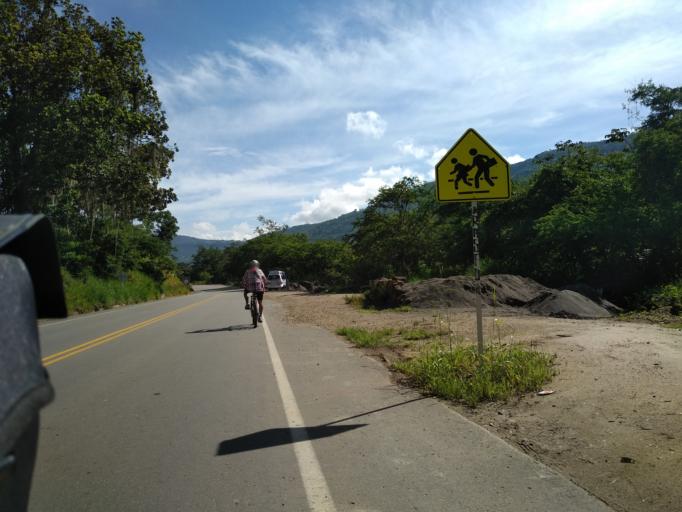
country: CO
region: Santander
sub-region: San Gil
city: San Gil
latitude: 6.5150
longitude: -73.1250
